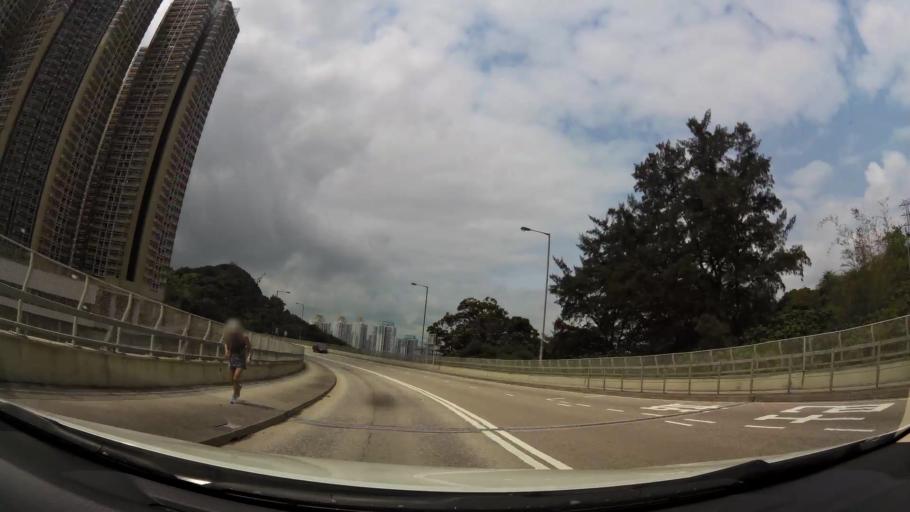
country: HK
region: Wong Tai Sin
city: Wong Tai Sin
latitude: 22.3338
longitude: 114.2222
